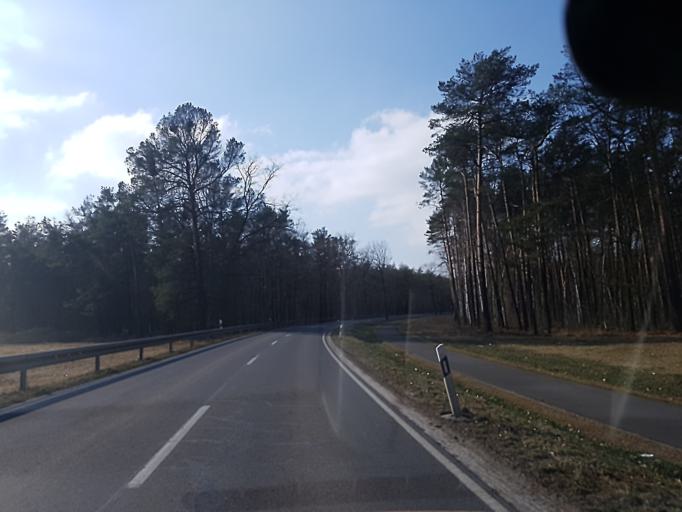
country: DE
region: Brandenburg
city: Doberlug-Kirchhain
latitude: 51.6312
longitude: 13.6018
